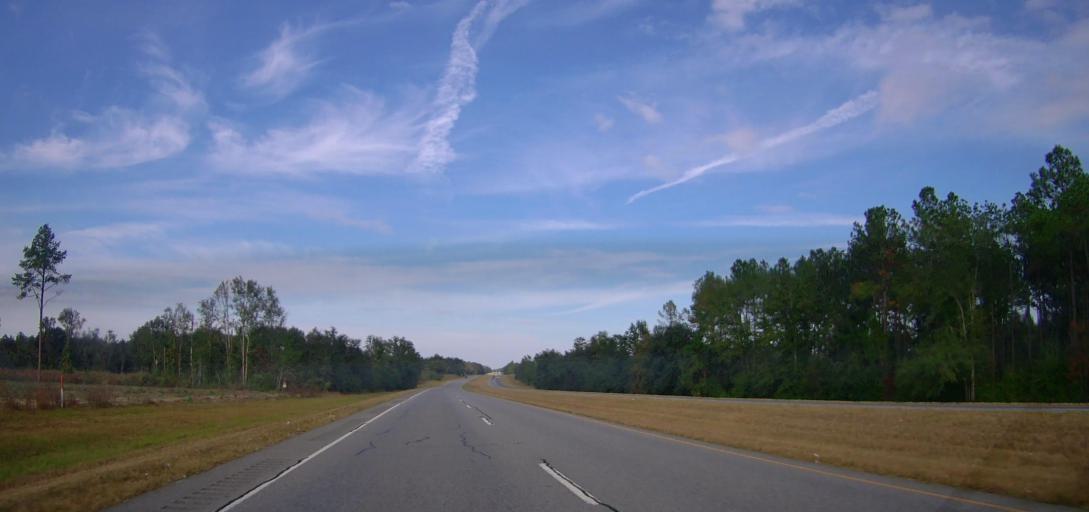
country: US
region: Georgia
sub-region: Mitchell County
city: Camilla
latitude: 31.2884
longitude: -84.1859
